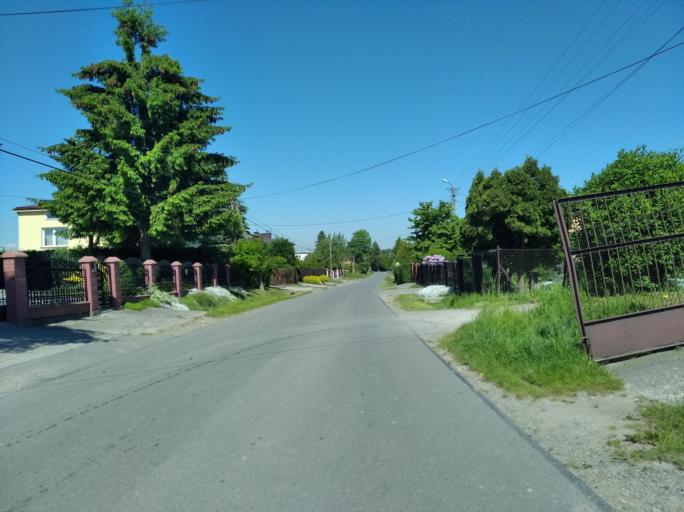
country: PL
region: Subcarpathian Voivodeship
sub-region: Powiat krosnienski
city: Korczyna
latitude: 49.7183
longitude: 21.7950
